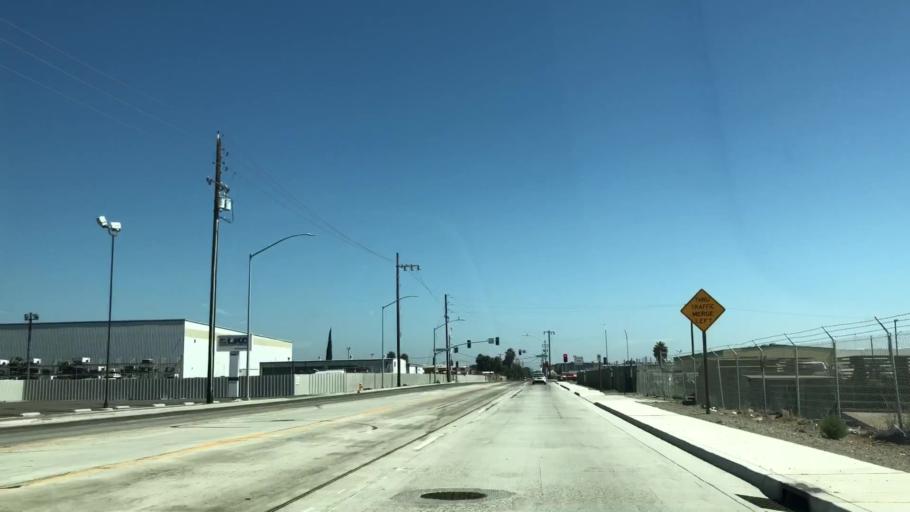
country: US
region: California
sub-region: San Joaquin County
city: Stockton
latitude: 37.9374
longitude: -121.3203
